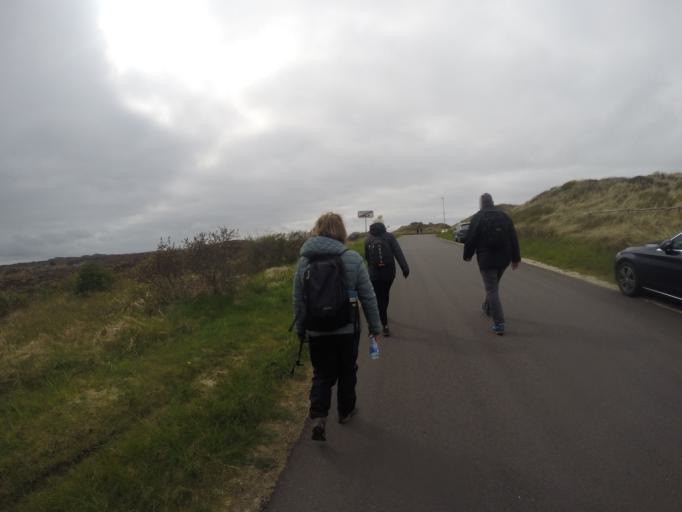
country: DK
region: North Denmark
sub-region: Thisted Kommune
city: Hurup
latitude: 56.9245
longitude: 8.3484
